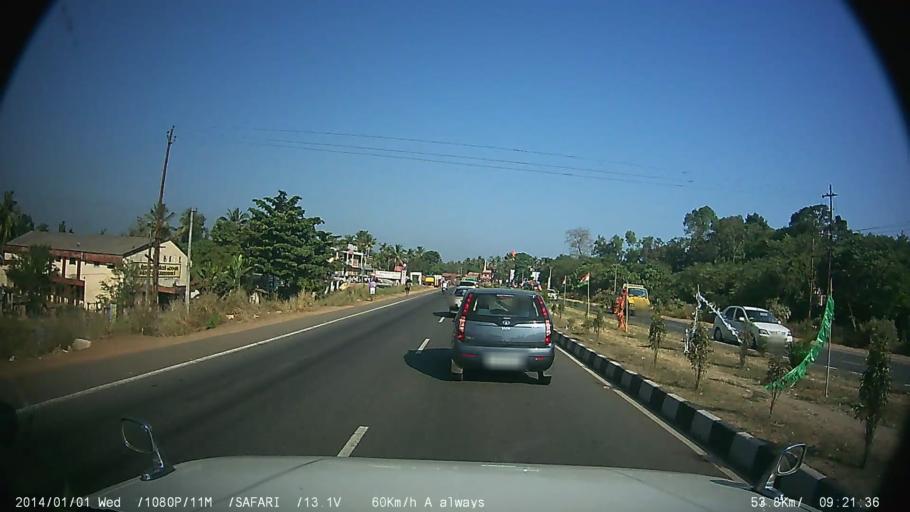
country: IN
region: Kerala
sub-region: Thrissur District
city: Kizhake Chalakudi
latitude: 10.2709
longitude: 76.3480
